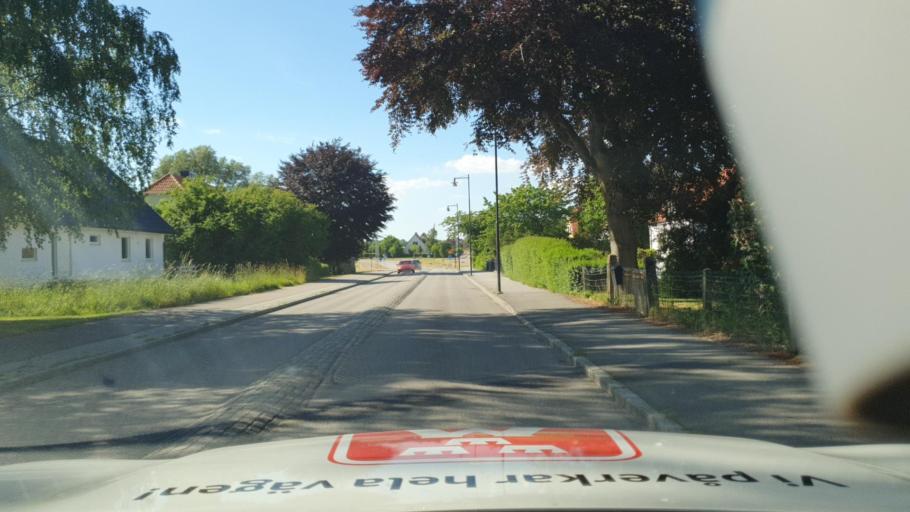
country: SE
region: Skane
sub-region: Skurups Kommun
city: Skurup
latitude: 55.4873
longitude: 13.4943
